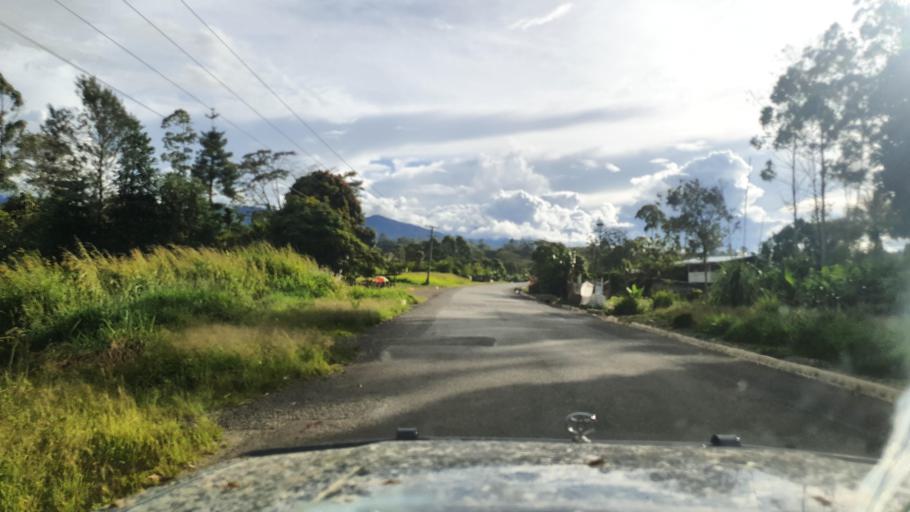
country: PG
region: Jiwaka
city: Minj
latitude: -5.8775
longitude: 144.7056
